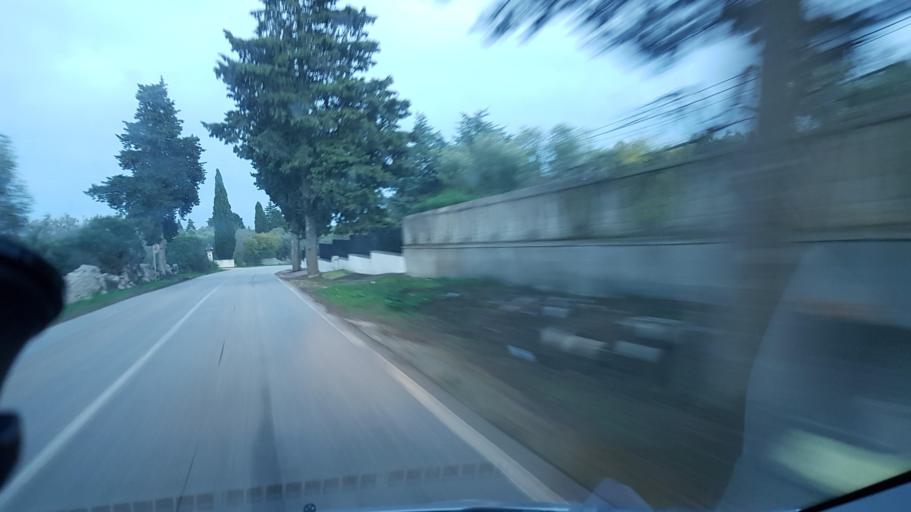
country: IT
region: Apulia
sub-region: Provincia di Brindisi
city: Ceglie Messapica
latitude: 40.6428
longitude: 17.5636
